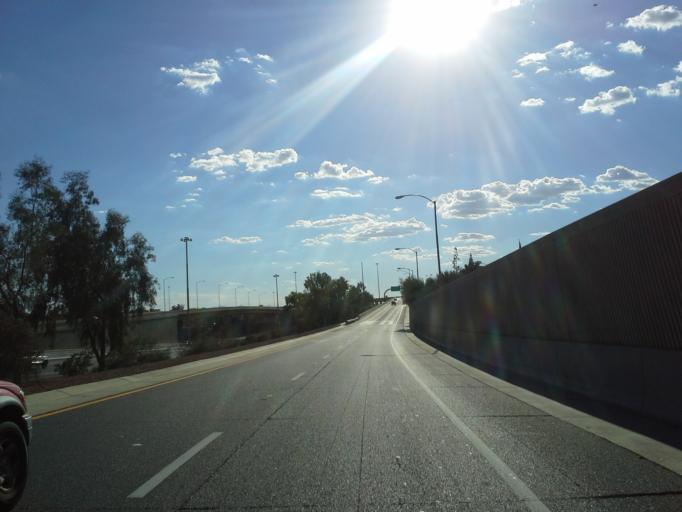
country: US
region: Arizona
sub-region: Maricopa County
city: Glendale
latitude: 33.6692
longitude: -112.1044
